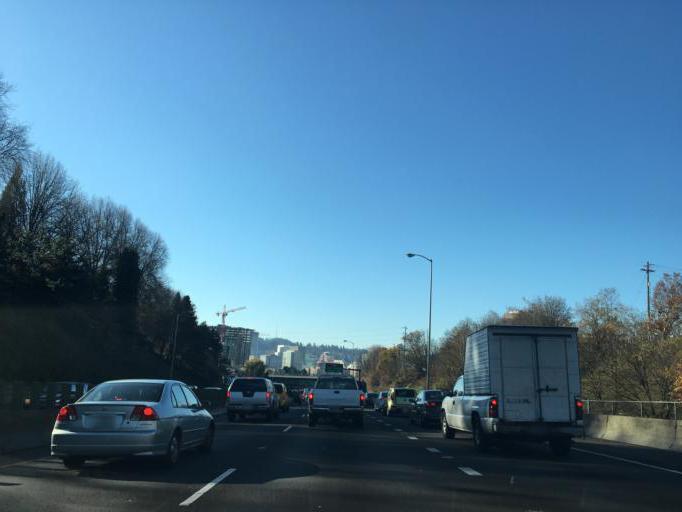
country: US
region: Oregon
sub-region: Multnomah County
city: Portland
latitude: 45.5276
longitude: -122.6568
